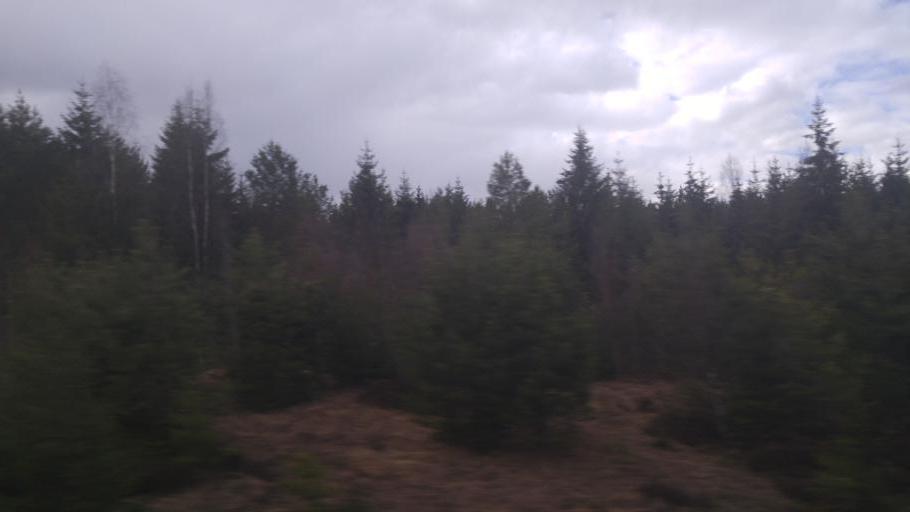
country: NO
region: Akershus
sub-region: Eidsvoll
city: Raholt
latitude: 60.2465
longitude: 11.1197
